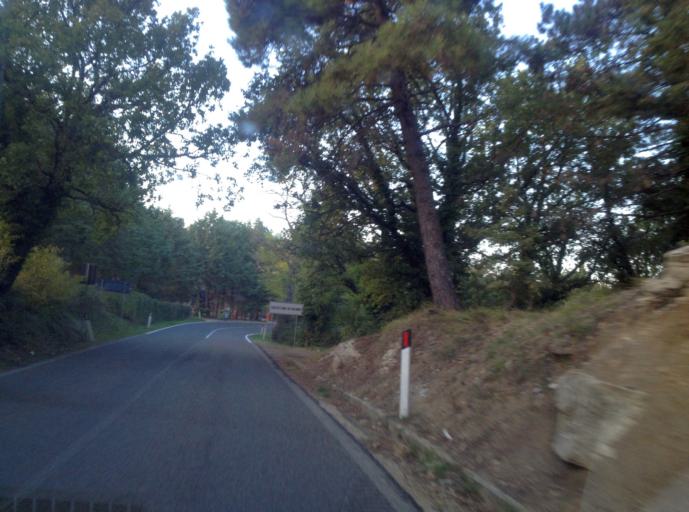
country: IT
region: Tuscany
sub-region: Provincia di Siena
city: Castellina in Chianti
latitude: 43.4514
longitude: 11.2927
